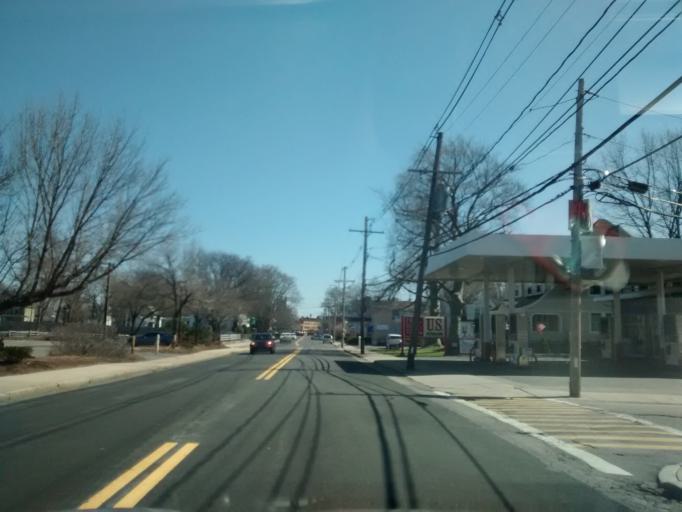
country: US
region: Massachusetts
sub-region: Middlesex County
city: Framingham
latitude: 42.2840
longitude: -71.4208
